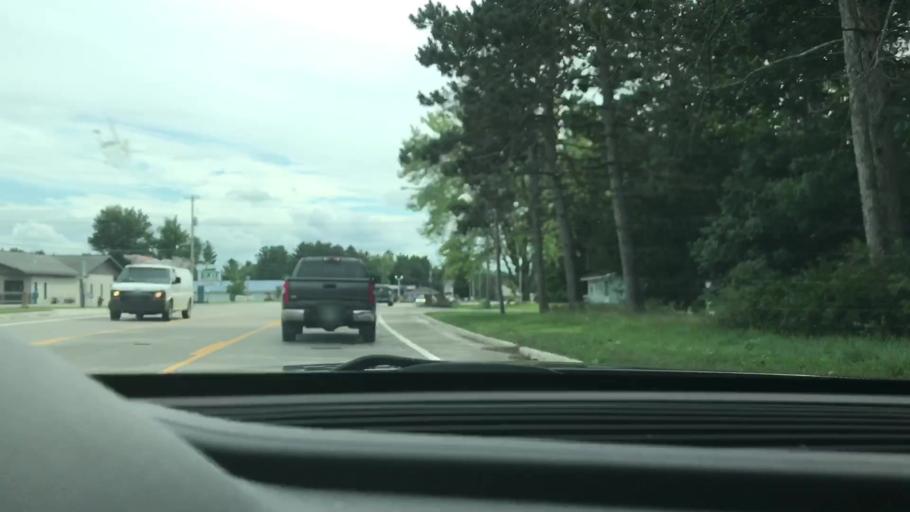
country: US
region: Michigan
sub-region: Missaukee County
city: Lake City
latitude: 44.3206
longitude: -85.2118
